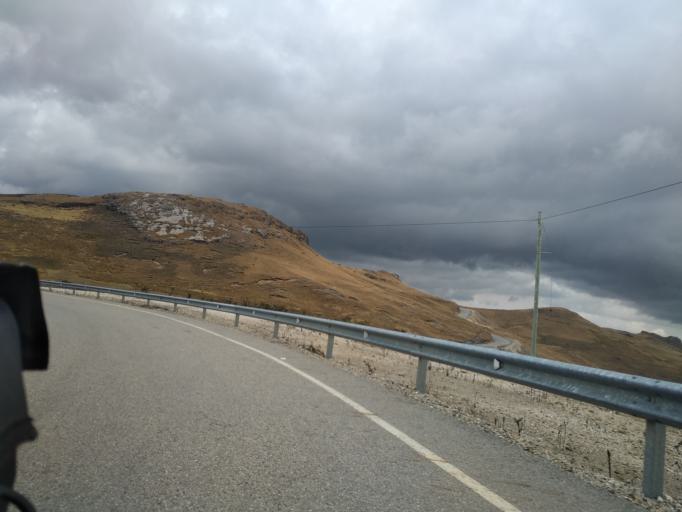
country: PE
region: La Libertad
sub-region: Provincia de Santiago de Chuco
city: Quiruvilca
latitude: -7.9883
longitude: -78.2775
